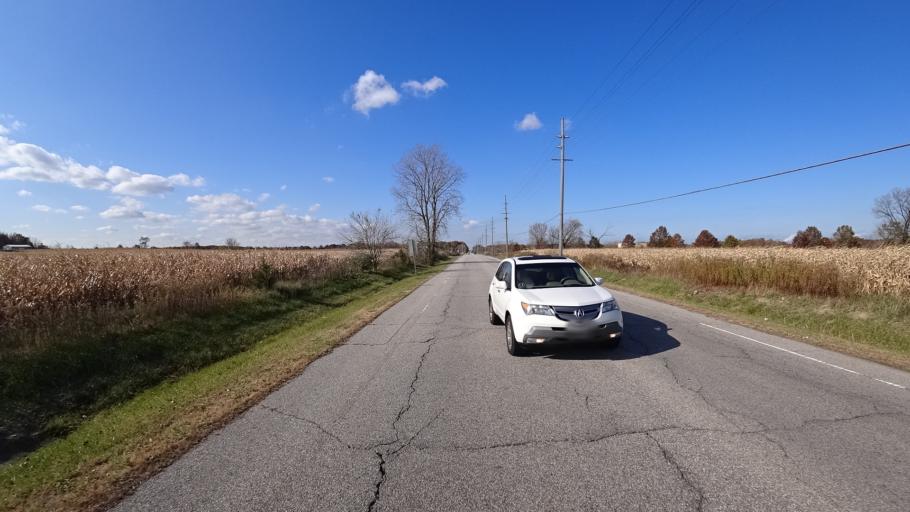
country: US
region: Indiana
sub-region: LaPorte County
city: Trail Creek
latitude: 41.6802
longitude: -86.8671
